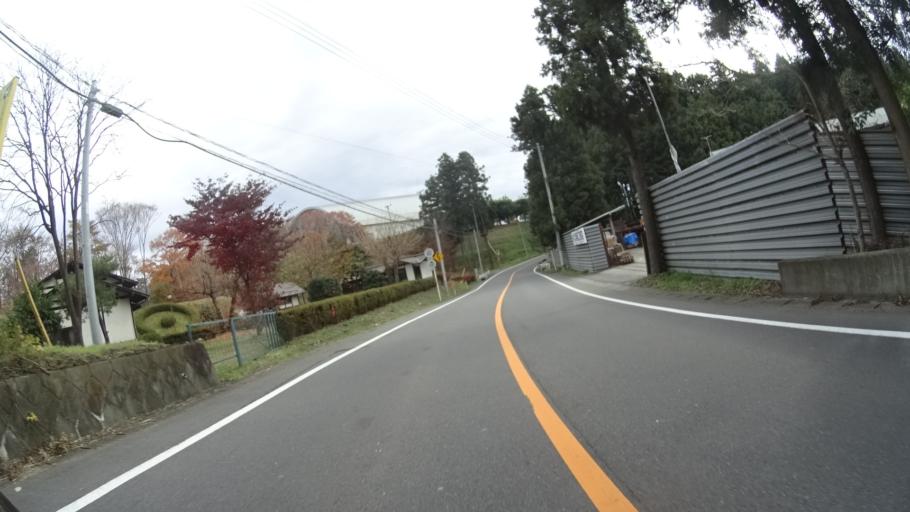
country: JP
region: Gunma
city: Shibukawa
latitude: 36.5370
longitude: 139.0532
